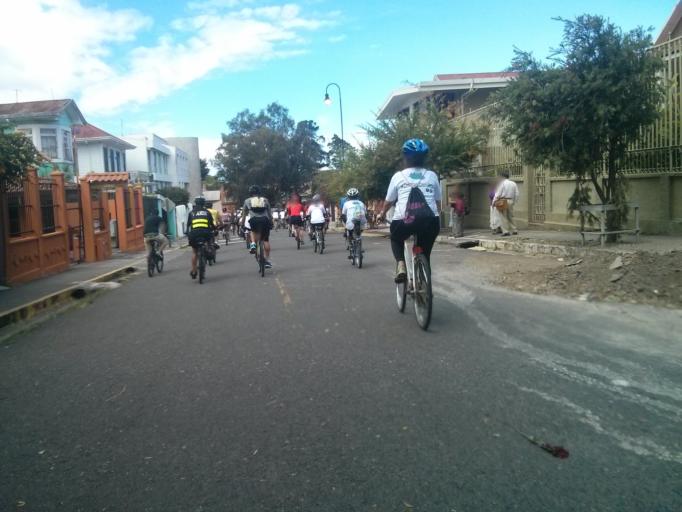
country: CR
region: San Jose
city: San Jose
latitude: 9.9379
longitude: -84.0713
